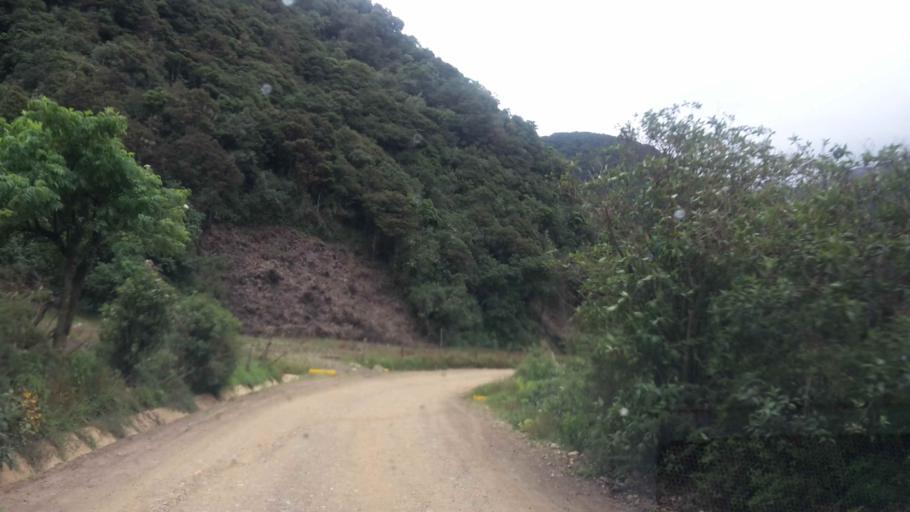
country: BO
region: Cochabamba
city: Totora
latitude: -17.5646
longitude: -65.2770
